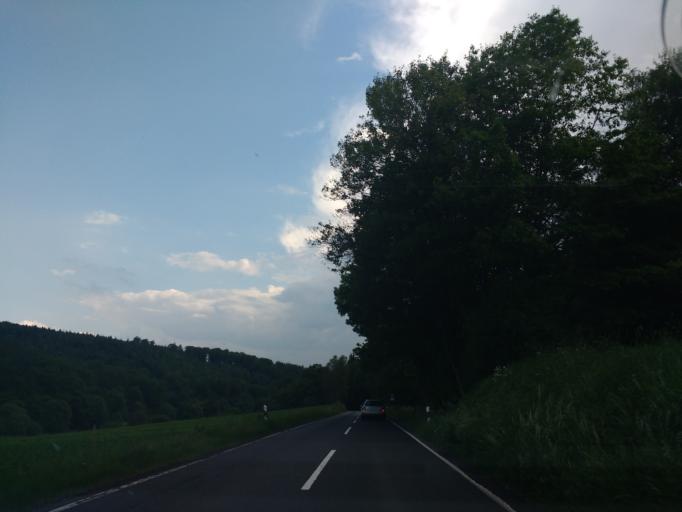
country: DE
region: Hesse
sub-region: Regierungsbezirk Giessen
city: Colbe
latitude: 50.9070
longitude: 8.8360
